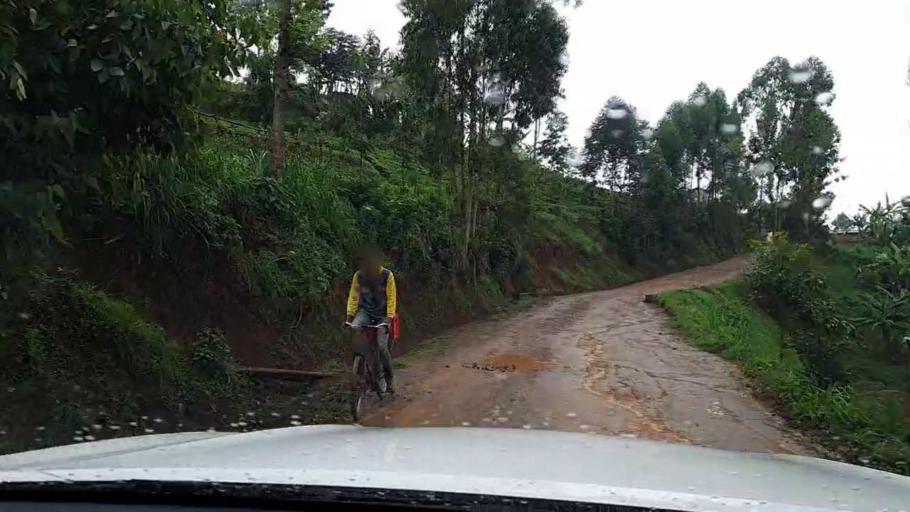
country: RW
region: Western Province
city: Cyangugu
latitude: -2.5441
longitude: 28.9774
